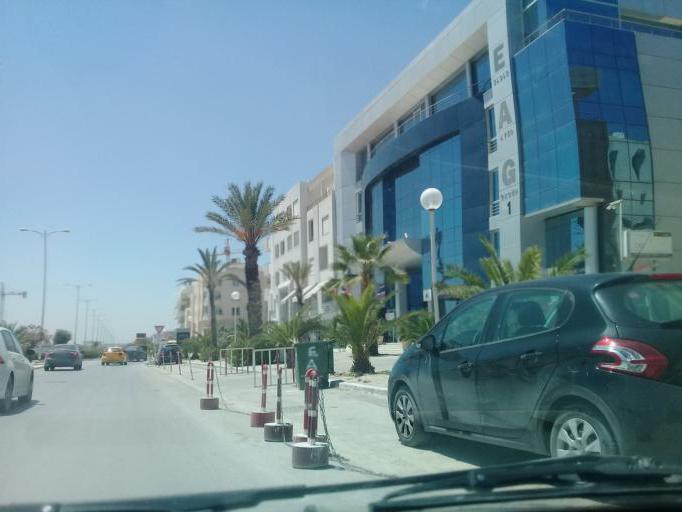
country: TN
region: Tunis
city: La Goulette
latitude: 36.8430
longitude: 10.2784
